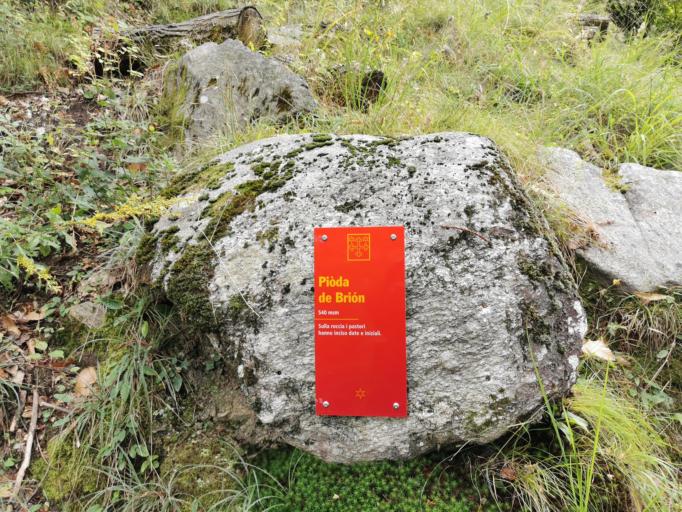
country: CH
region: Grisons
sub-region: Moesa District
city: Santa Maria in Calanca
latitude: 46.2697
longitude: 9.1786
